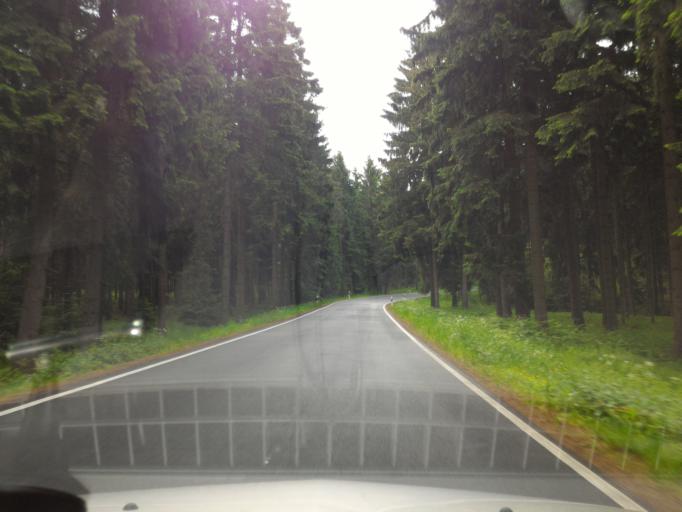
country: DE
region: Saxony
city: Kurort Oybin
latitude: 50.8321
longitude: 14.7796
